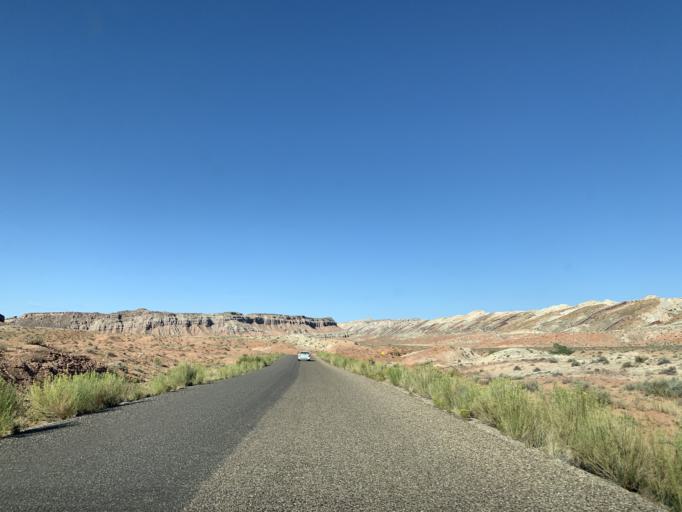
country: US
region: Utah
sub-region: Emery County
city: Ferron
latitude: 38.5827
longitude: -110.7999
